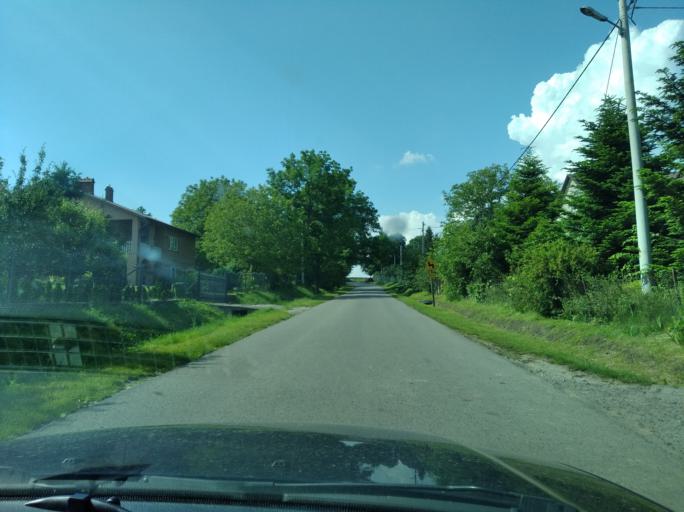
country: PL
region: Subcarpathian Voivodeship
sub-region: Powiat jaroslawski
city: Rokietnica
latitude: 49.9246
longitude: 22.6852
